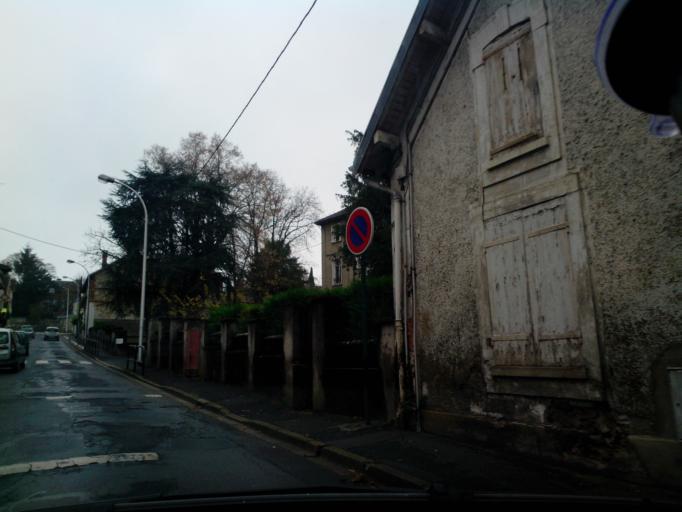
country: FR
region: Ile-de-France
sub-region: Departement de l'Essonne
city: Evry
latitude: 48.6343
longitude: 2.4478
